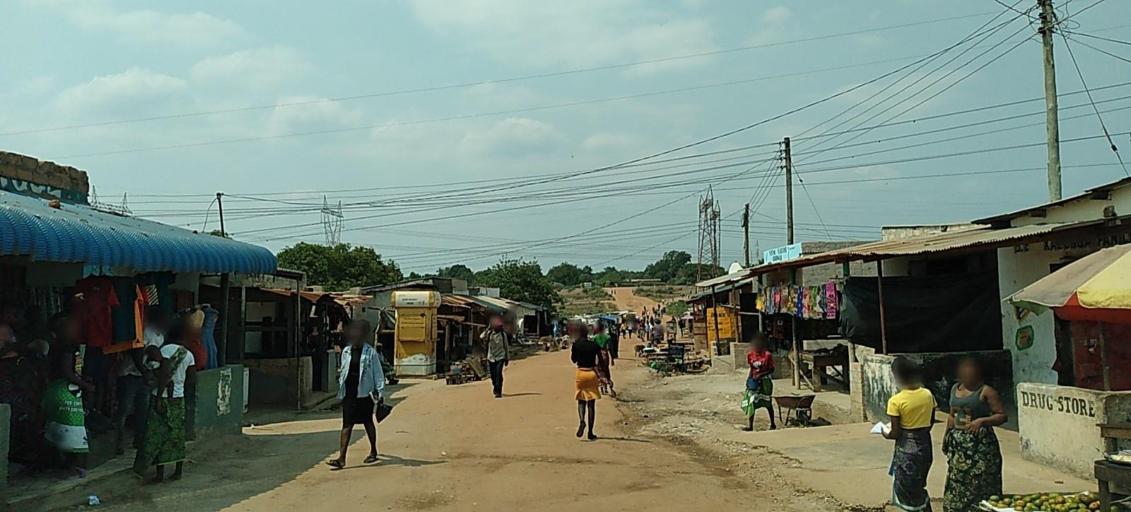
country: ZM
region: Copperbelt
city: Chambishi
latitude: -12.6324
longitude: 28.0702
